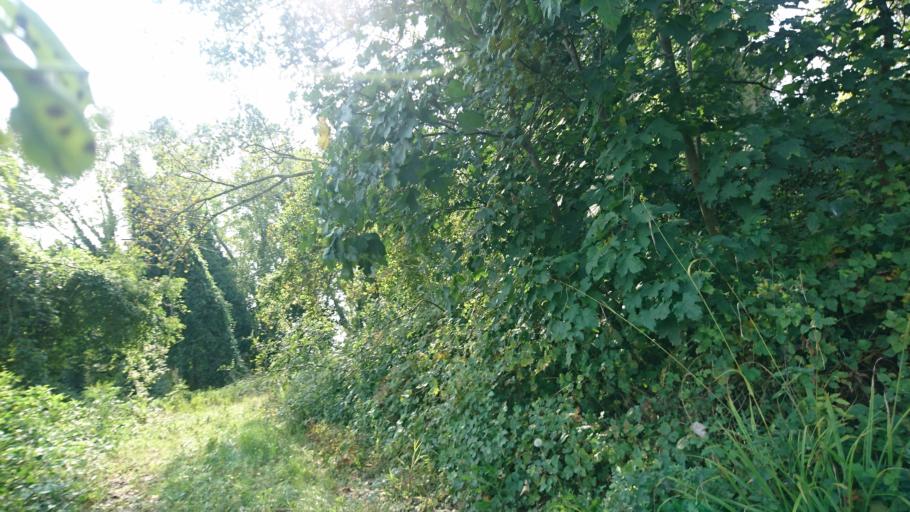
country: IT
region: Veneto
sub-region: Provincia di Padova
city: Piazzola sul Brenta
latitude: 45.5713
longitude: 11.7671
